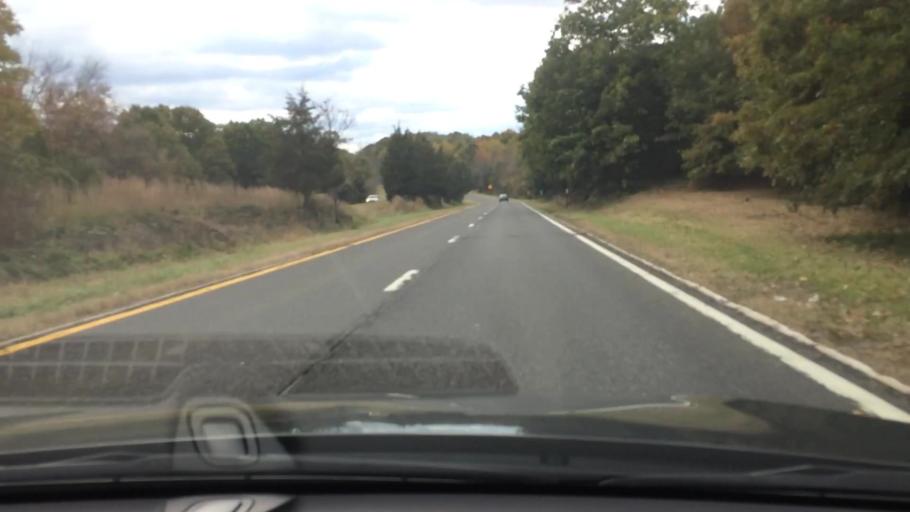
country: US
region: New York
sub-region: Dutchess County
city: Pleasant Valley
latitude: 41.7090
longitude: -73.7829
